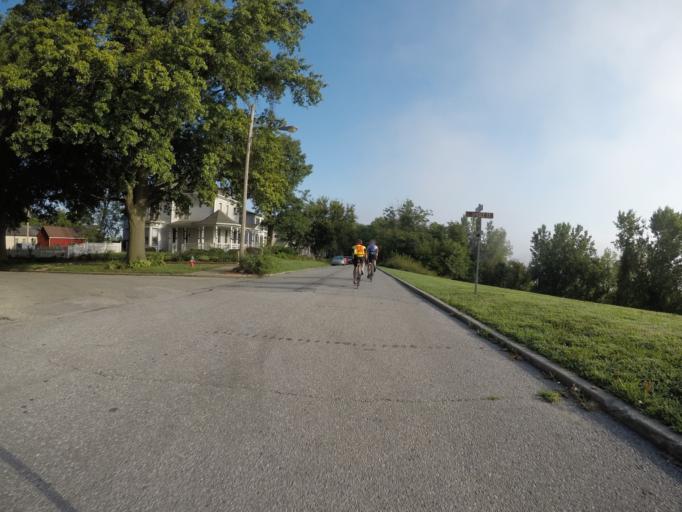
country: US
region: Kansas
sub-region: Leavenworth County
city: Leavenworth
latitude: 39.3113
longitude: -94.9077
